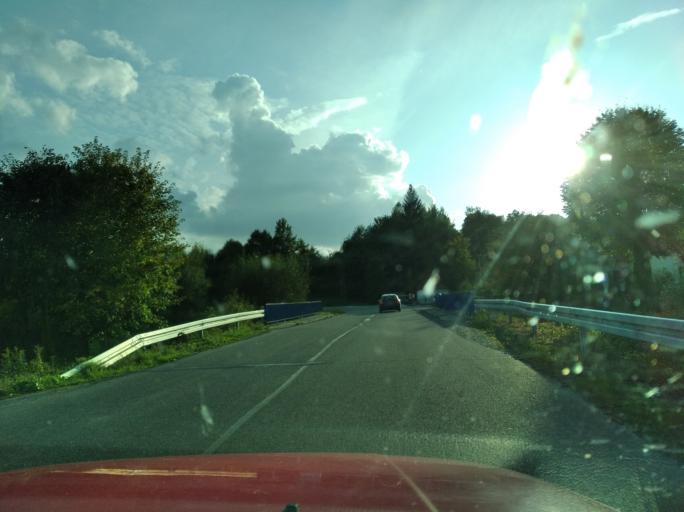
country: PL
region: Subcarpathian Voivodeship
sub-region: Powiat przemyski
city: Nienadowa
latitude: 49.8348
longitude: 22.4334
